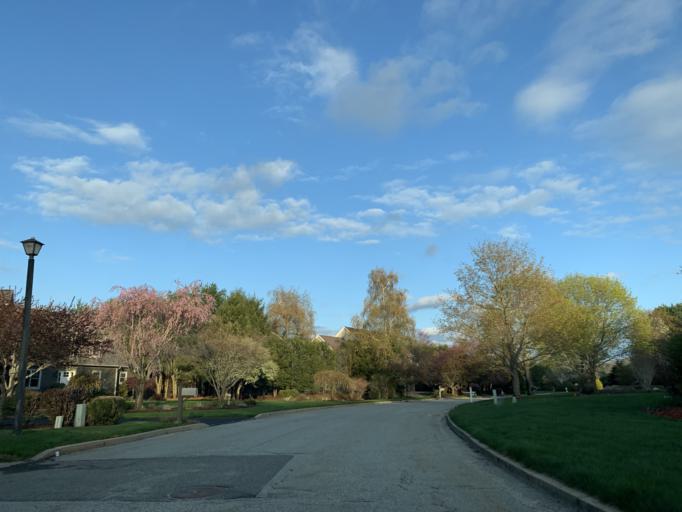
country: US
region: Rhode Island
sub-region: Providence County
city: Valley Falls
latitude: 41.9105
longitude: -71.4370
